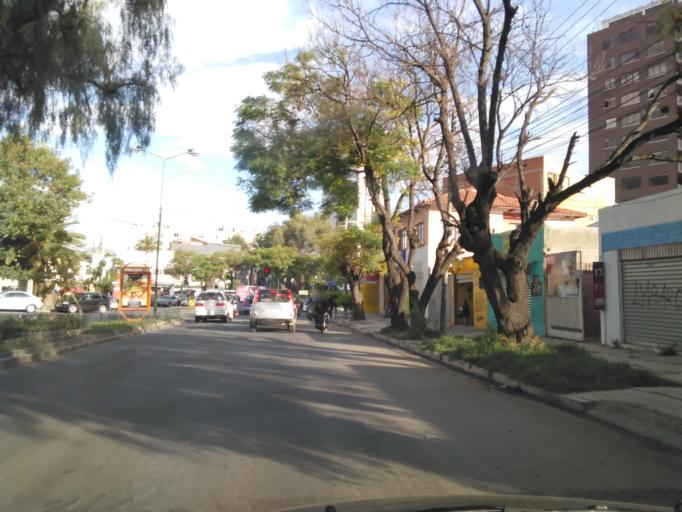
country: BO
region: Cochabamba
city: Cochabamba
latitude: -17.3678
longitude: -66.1645
